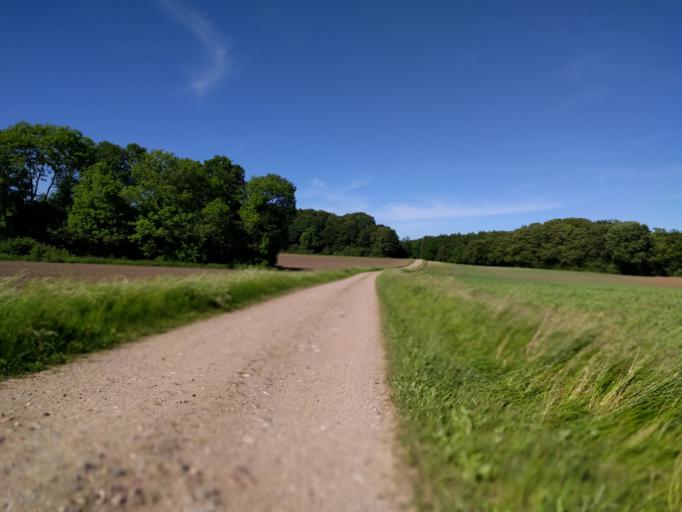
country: DK
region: South Denmark
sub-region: Kerteminde Kommune
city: Kerteminde
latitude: 55.4333
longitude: 10.6678
